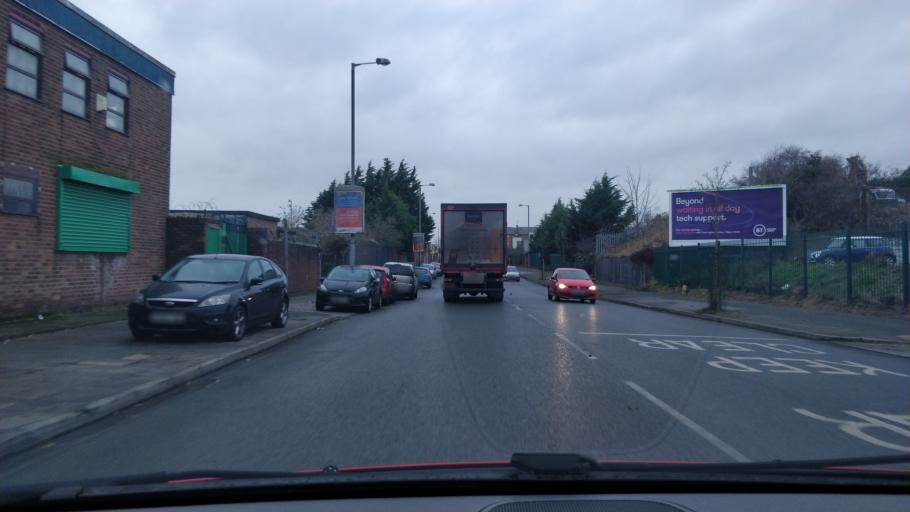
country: GB
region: England
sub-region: Sefton
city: Litherland
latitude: 53.4576
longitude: -2.9845
